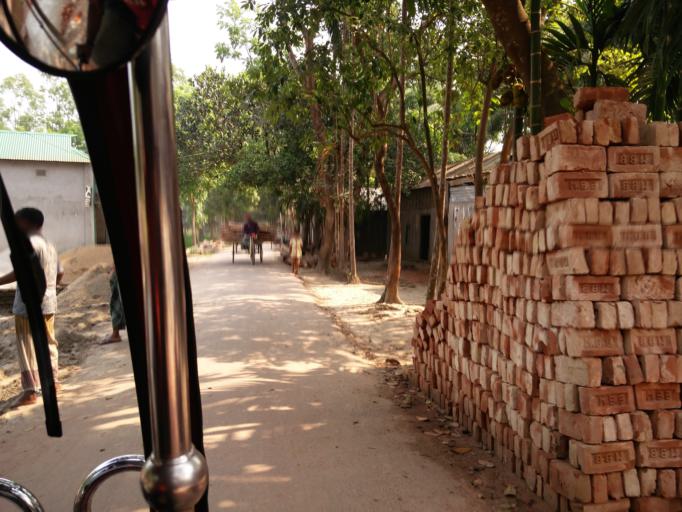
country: BD
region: Dhaka
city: Muktagacha
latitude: 24.9129
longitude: 90.2158
